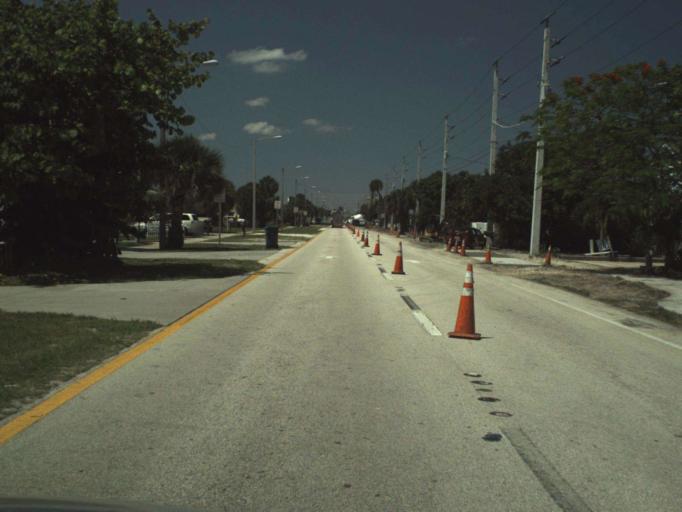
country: US
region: Florida
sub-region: Brevard County
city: Cocoa Beach
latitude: 28.3131
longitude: -80.6089
